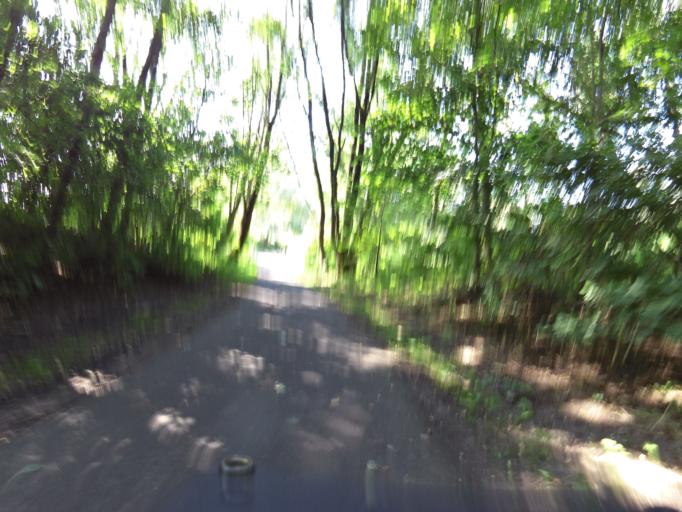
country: NL
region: South Holland
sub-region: Gemeente Barendrecht
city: Barendrecht
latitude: 51.8258
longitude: 4.5203
